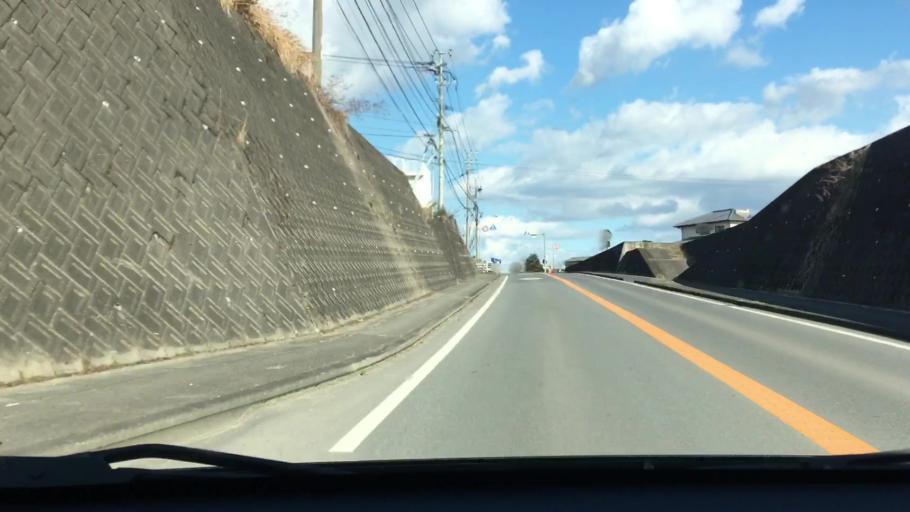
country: JP
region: Oita
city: Oita
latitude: 33.1740
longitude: 131.6575
